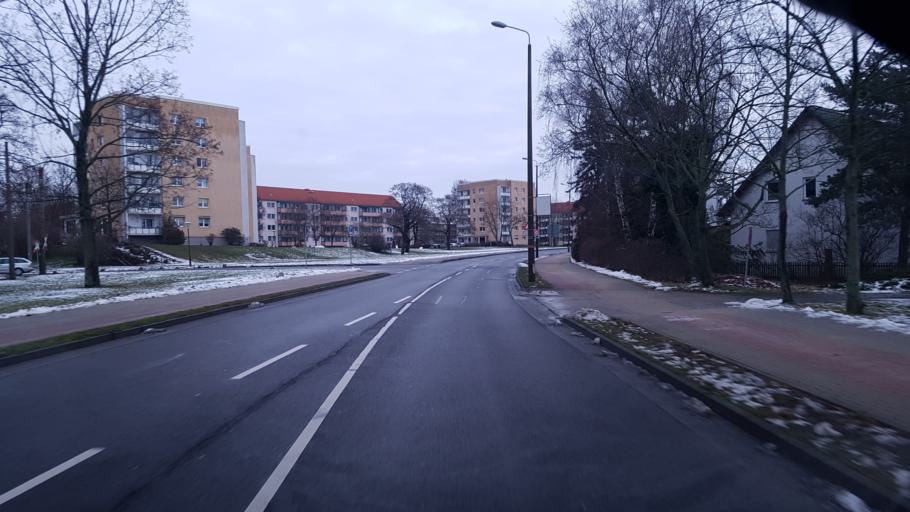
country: DE
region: Brandenburg
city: Cottbus
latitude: 51.7374
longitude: 14.3255
